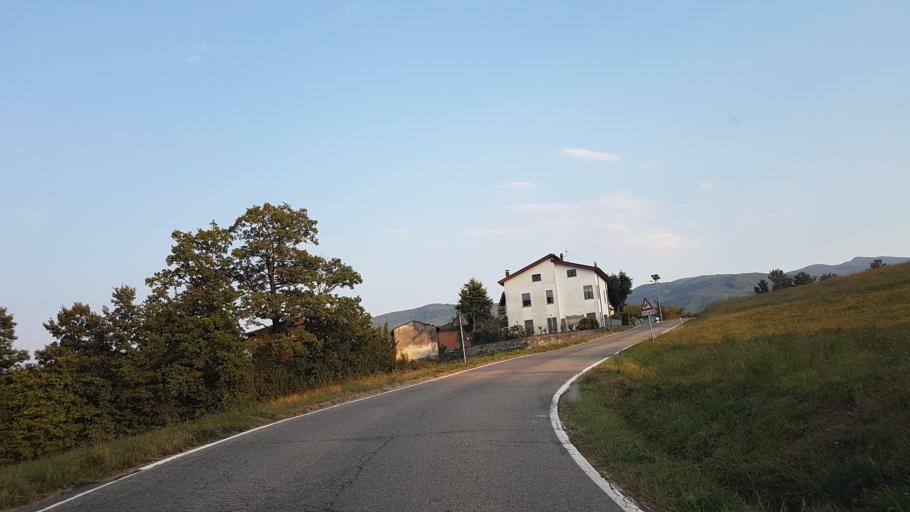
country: IT
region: Emilia-Romagna
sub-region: Provincia di Parma
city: Albareto
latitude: 44.4721
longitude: 9.7082
